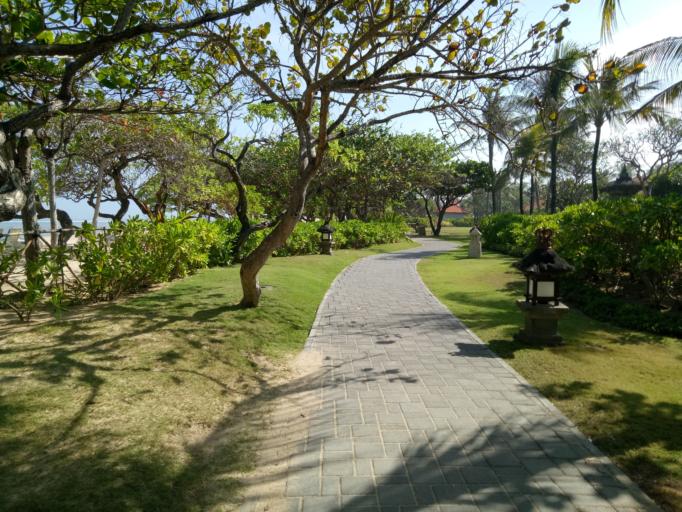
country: ID
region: Bali
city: Bualu
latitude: -8.8028
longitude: 115.2360
